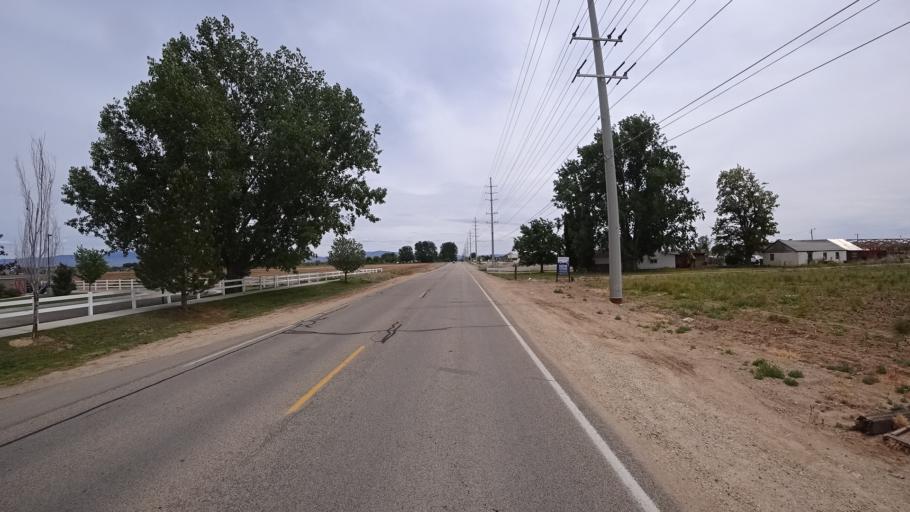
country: US
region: Idaho
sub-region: Ada County
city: Meridian
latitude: 43.5612
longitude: -116.3498
